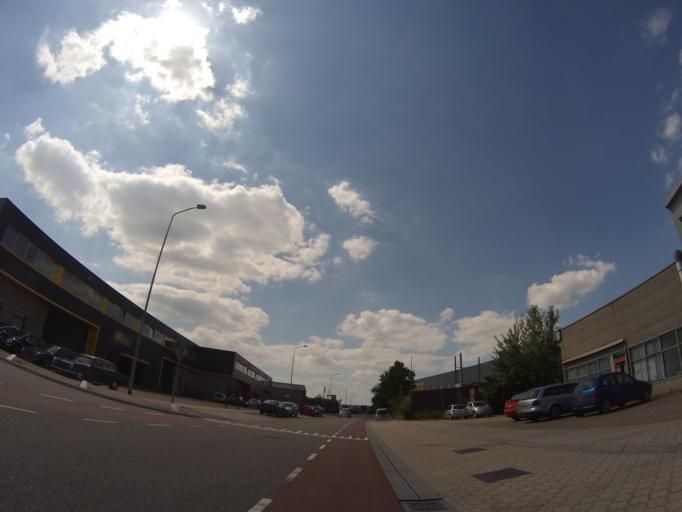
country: NL
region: Gelderland
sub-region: Gemeente Barneveld
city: Barneveld
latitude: 52.1639
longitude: 5.5843
